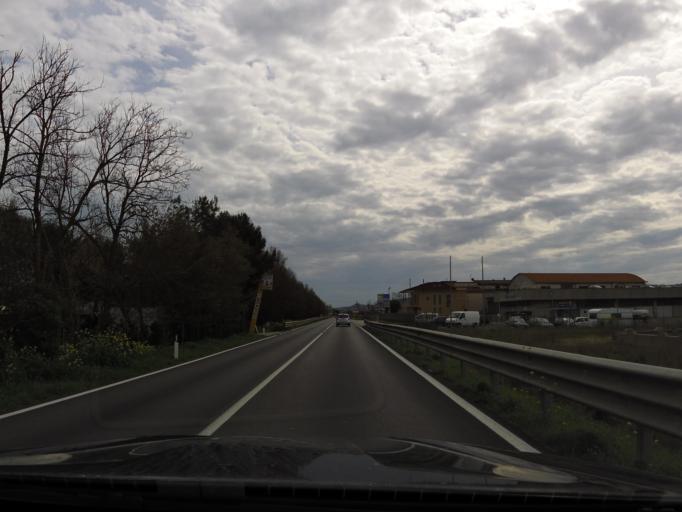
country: IT
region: The Marches
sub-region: Provincia di Macerata
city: Porto Recanati
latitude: 43.4044
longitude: 13.6776
